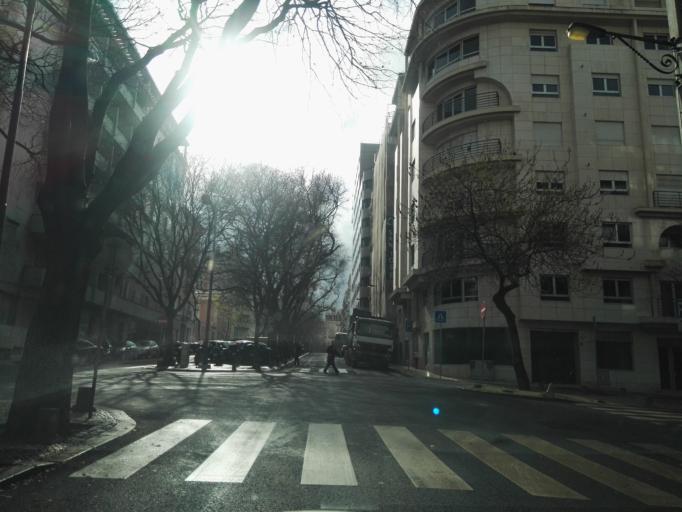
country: PT
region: Lisbon
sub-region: Lisbon
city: Lisbon
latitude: 38.7344
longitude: -9.1495
